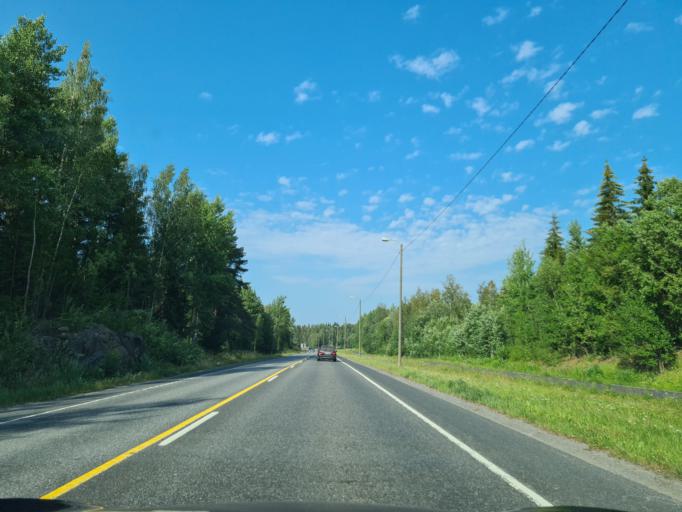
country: FI
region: Satakunta
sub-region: Pori
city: Pori
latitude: 61.5322
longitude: 21.8059
